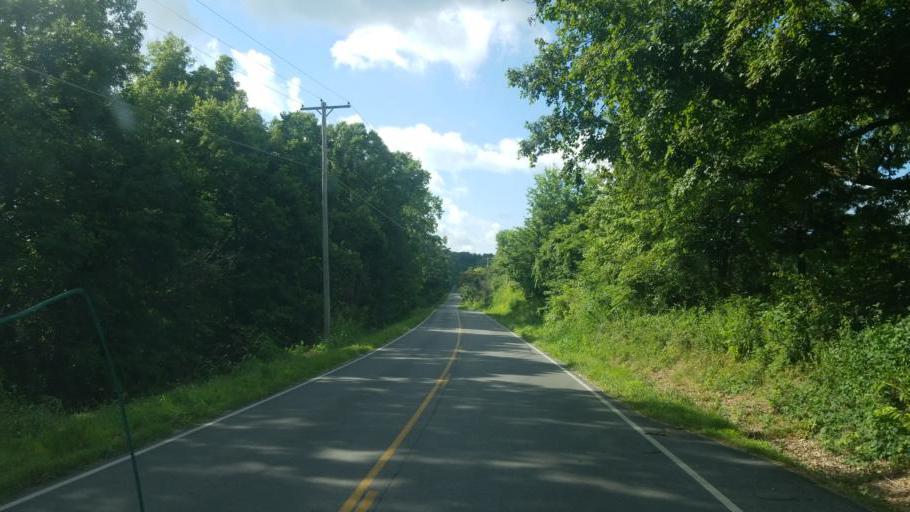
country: US
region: Illinois
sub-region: Union County
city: Cobden
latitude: 37.5639
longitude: -89.3094
